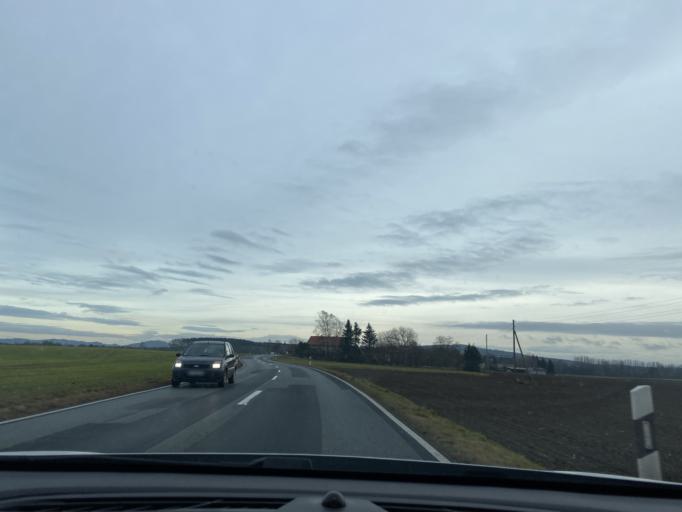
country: DE
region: Saxony
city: Reichenbach
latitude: 51.1213
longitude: 14.8255
